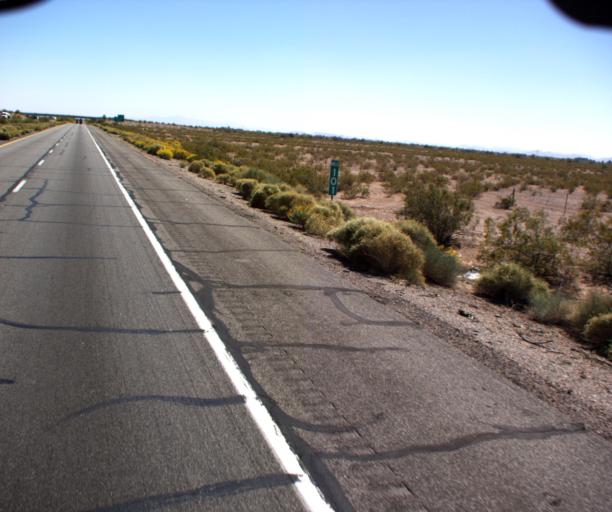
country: US
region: Arizona
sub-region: Maricopa County
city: Buckeye
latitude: 33.4717
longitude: -112.8228
